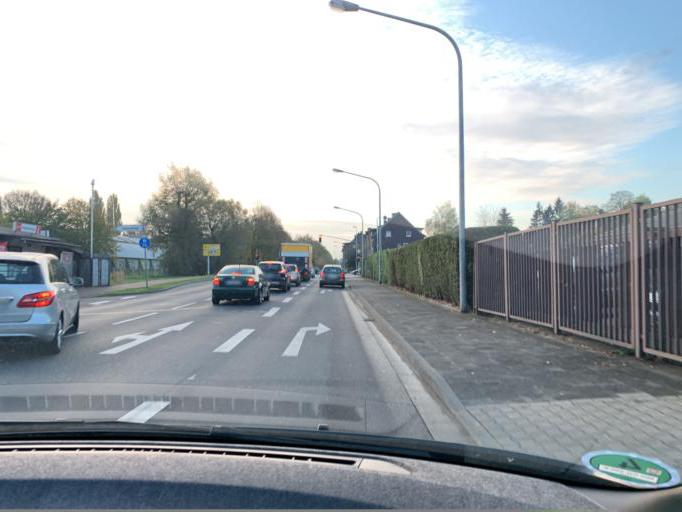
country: DE
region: North Rhine-Westphalia
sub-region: Regierungsbezirk Dusseldorf
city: Monchengladbach
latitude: 51.1480
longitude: 6.4500
